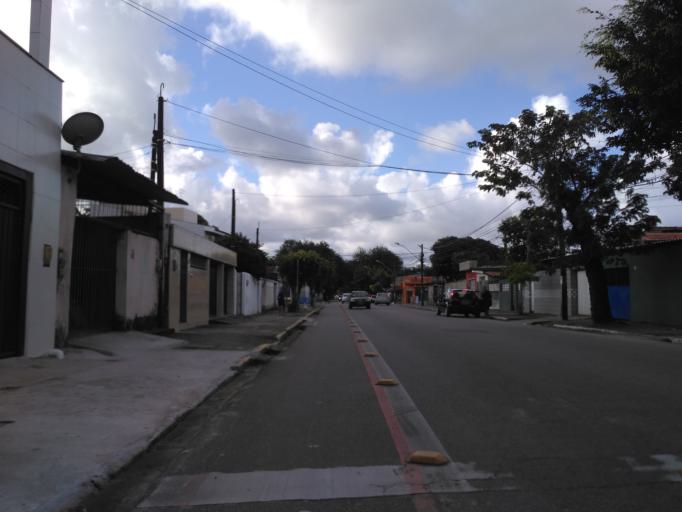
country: BR
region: Pernambuco
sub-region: Recife
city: Recife
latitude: -8.0556
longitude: -34.9419
